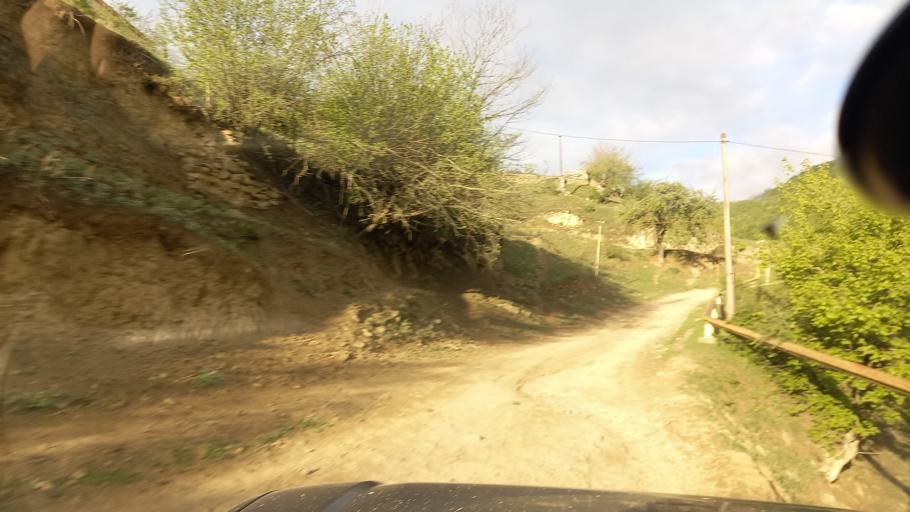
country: RU
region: Dagestan
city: Khuchni
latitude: 41.9481
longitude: 47.8342
